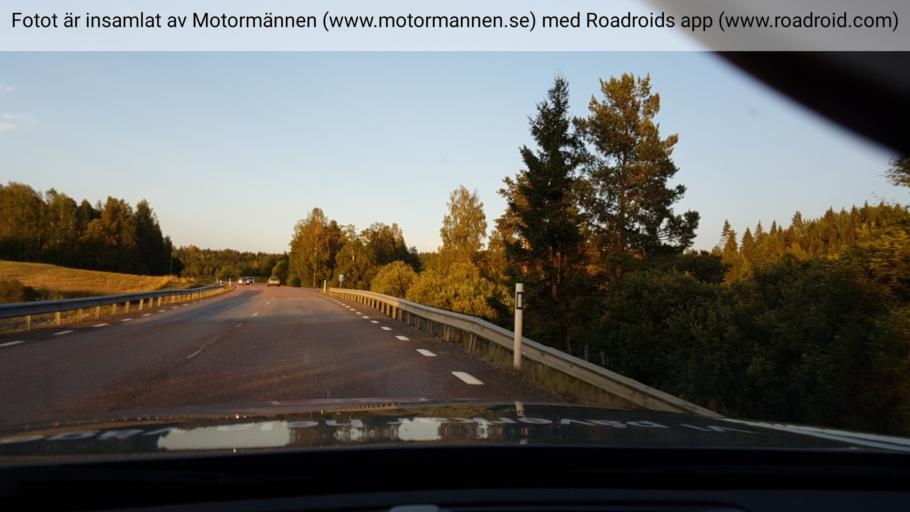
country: SE
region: Dalarna
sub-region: Smedjebackens Kommun
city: Smedjebacken
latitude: 60.1290
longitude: 15.4186
